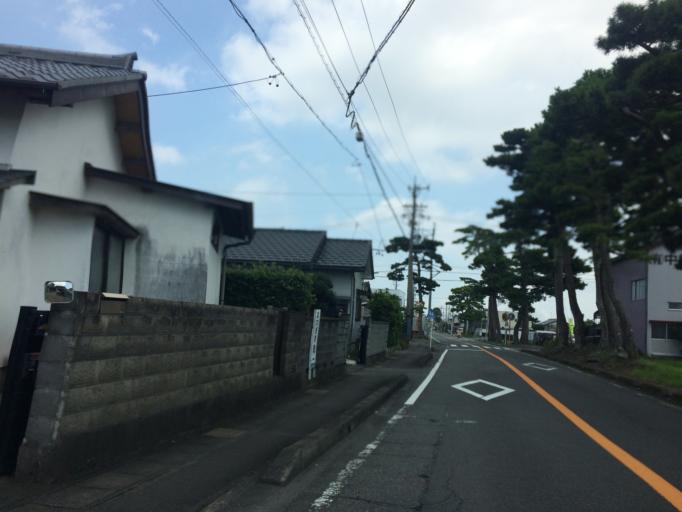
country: JP
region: Shizuoka
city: Shimada
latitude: 34.8420
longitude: 138.2193
